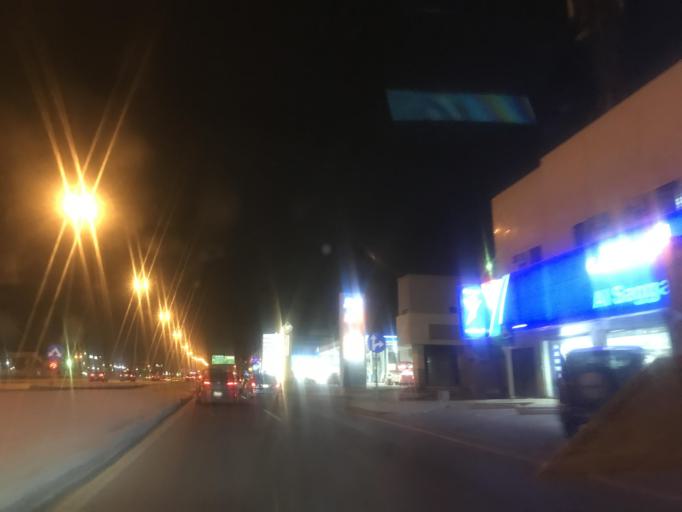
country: SA
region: Ar Riyad
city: Riyadh
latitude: 24.7753
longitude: 46.7282
